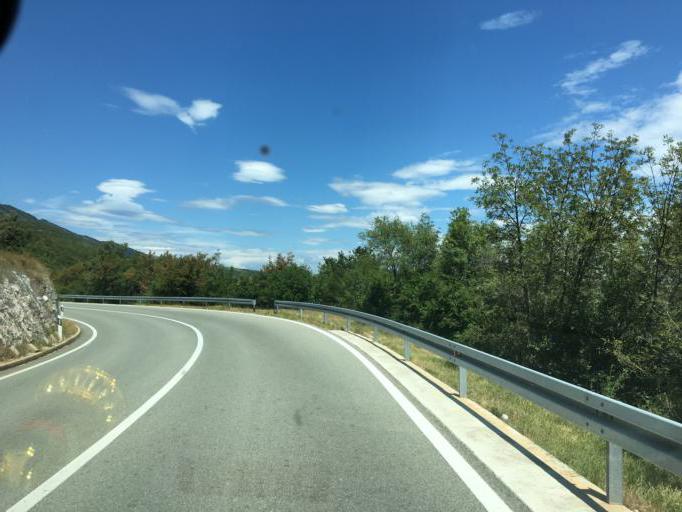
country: HR
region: Istarska
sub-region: Grad Labin
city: Rabac
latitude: 45.1443
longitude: 14.2128
